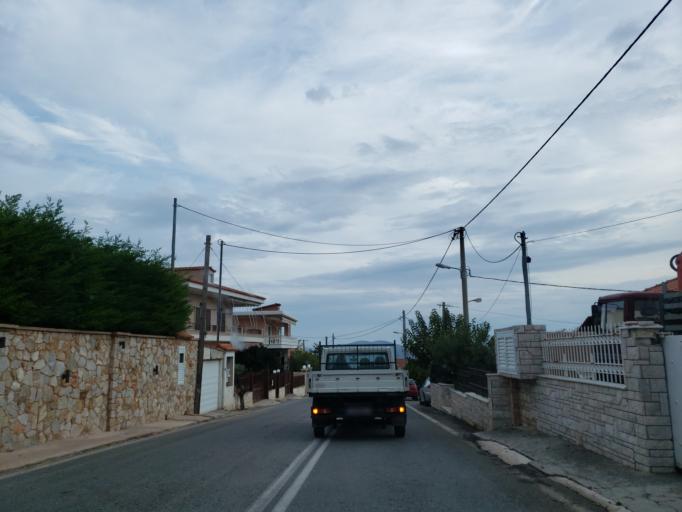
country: GR
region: Attica
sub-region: Nomarchia Anatolikis Attikis
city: Grammatiko
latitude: 38.2042
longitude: 23.9623
